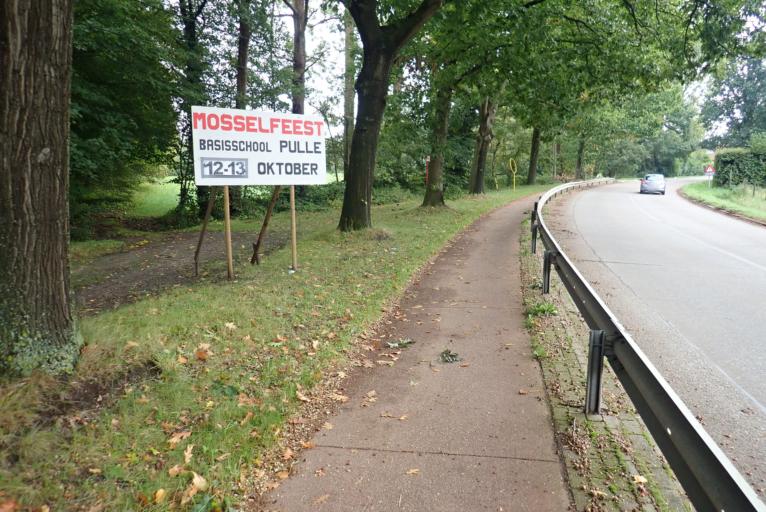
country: BE
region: Flanders
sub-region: Provincie Antwerpen
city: Grobbendonk
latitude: 51.2095
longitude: 4.7074
